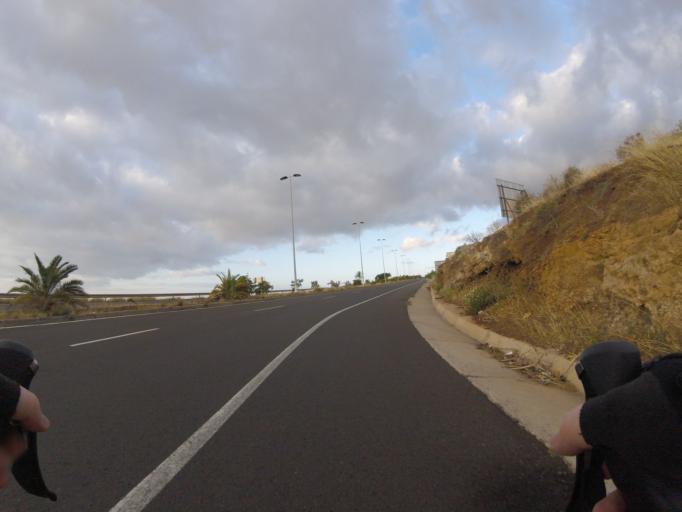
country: ES
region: Canary Islands
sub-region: Provincia de Santa Cruz de Tenerife
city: La Laguna
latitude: 28.4302
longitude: -16.3119
